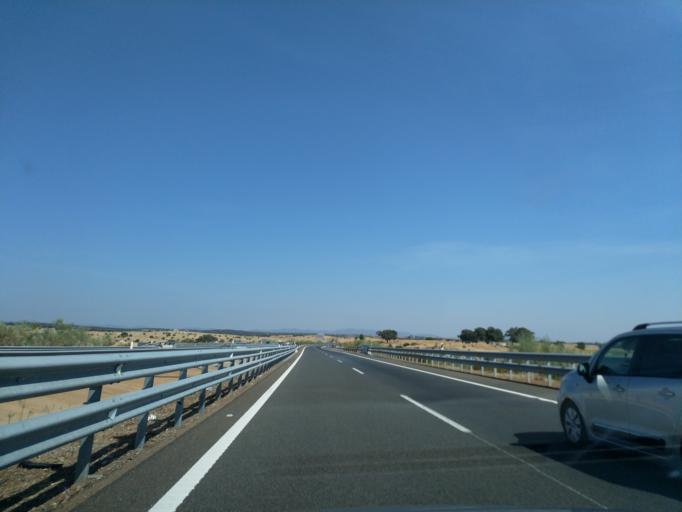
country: ES
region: Extremadura
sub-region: Provincia de Badajoz
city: Mirandilla
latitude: 38.9763
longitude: -6.3343
